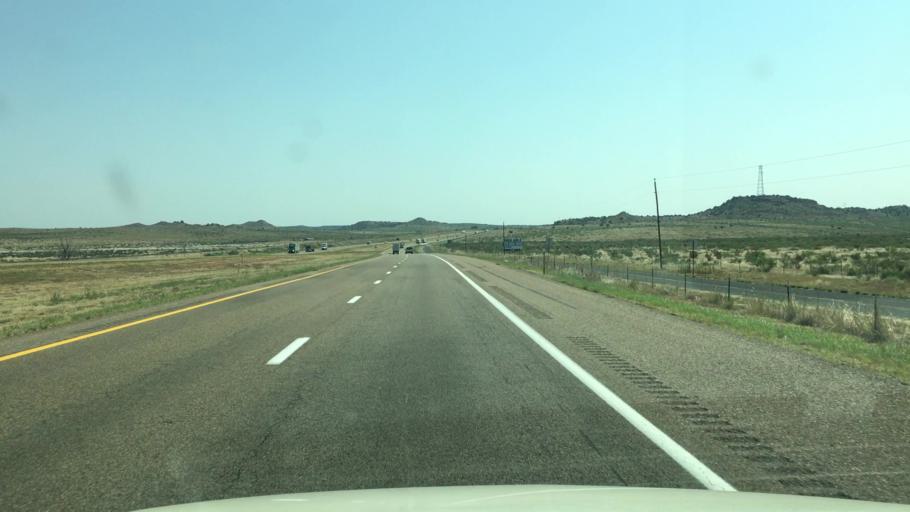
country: US
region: New Mexico
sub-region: Quay County
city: Tucumcari
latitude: 35.1225
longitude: -103.9639
